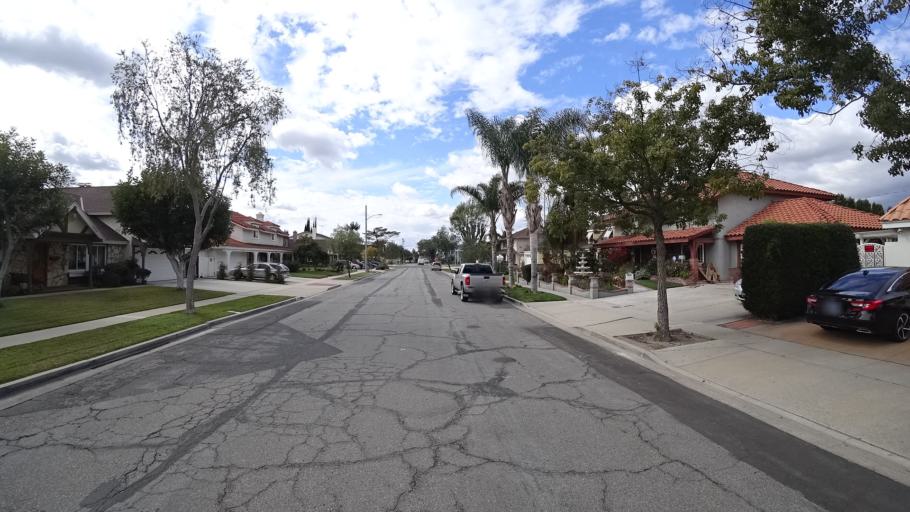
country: US
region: California
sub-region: Orange County
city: Placentia
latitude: 33.8392
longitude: -117.8656
